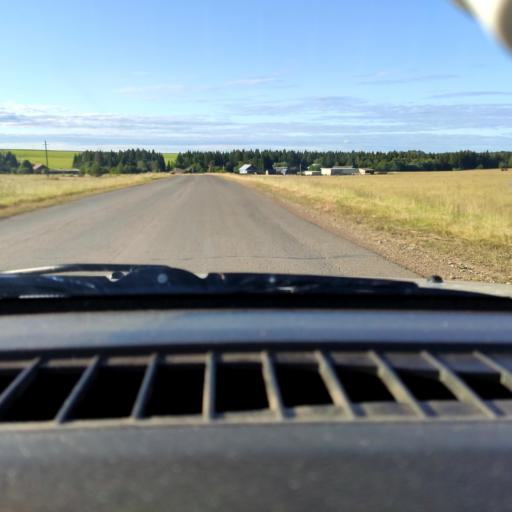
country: RU
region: Perm
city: Uinskoye
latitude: 57.0759
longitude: 56.5578
